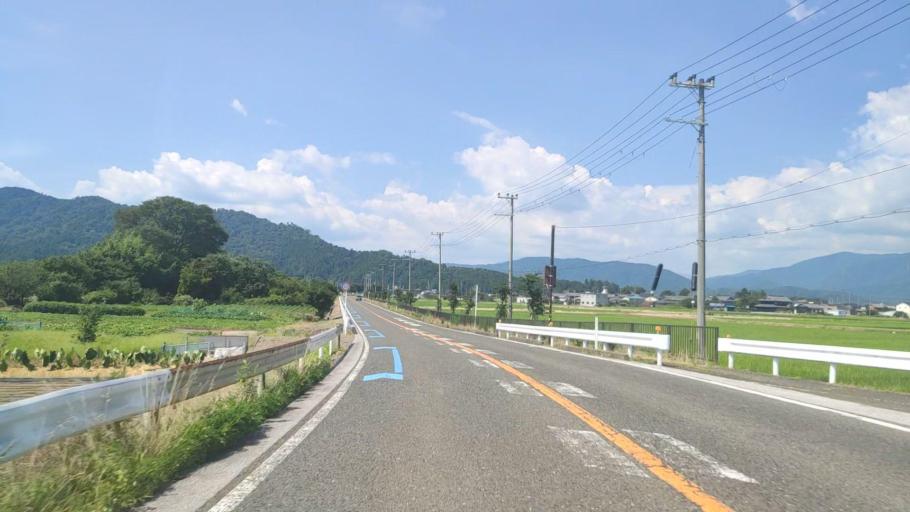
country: JP
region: Shiga Prefecture
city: Nagahama
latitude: 35.4630
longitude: 136.2063
